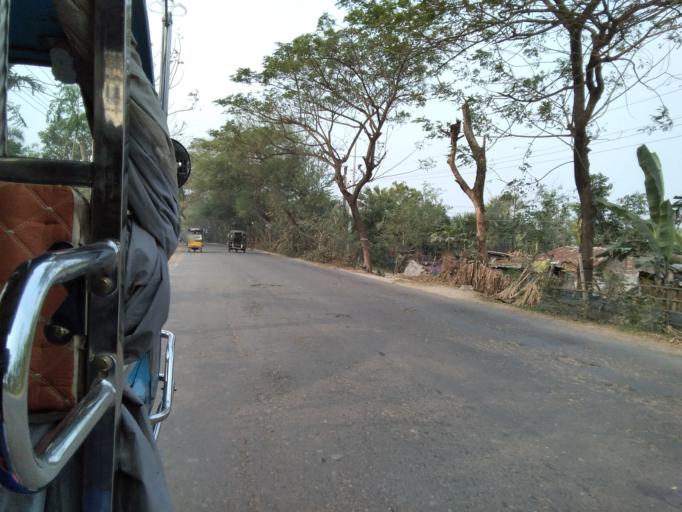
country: BD
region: Khulna
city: Satkhira
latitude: 22.6904
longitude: 89.0381
